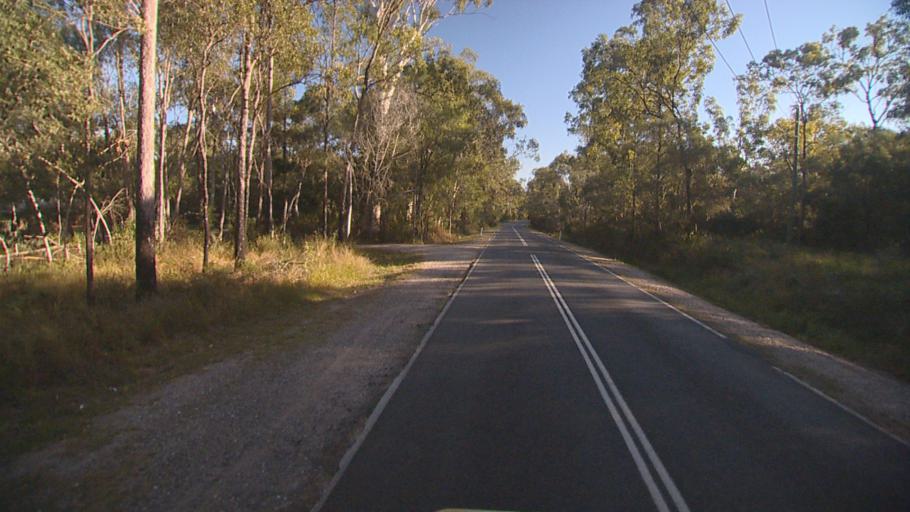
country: AU
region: Queensland
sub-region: Logan
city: Chambers Flat
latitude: -27.7776
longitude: 153.0746
